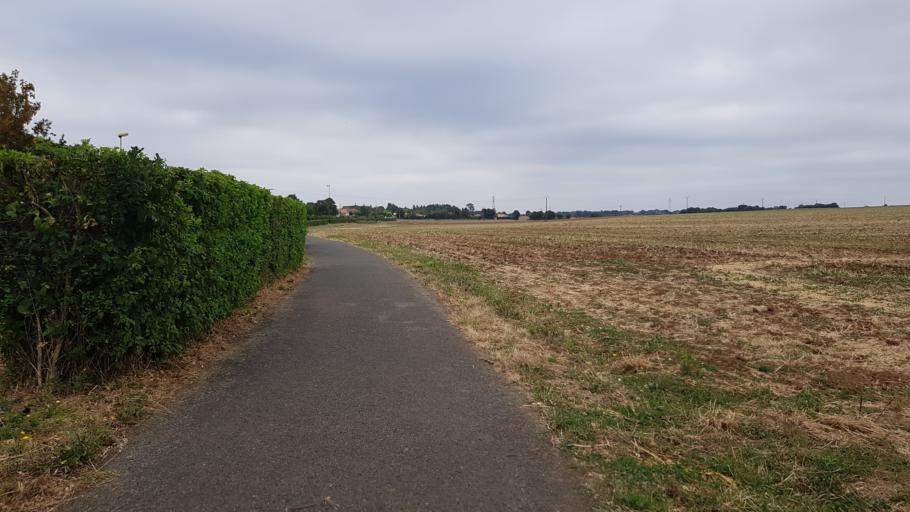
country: FR
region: Poitou-Charentes
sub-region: Departement des Deux-Sevres
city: Vouille
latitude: 46.3218
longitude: -0.3524
